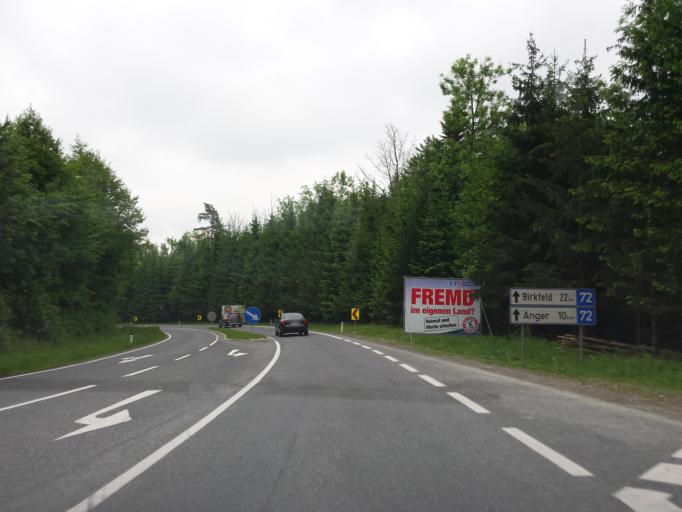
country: AT
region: Styria
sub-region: Politischer Bezirk Weiz
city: Unterfladnitz
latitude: 47.2189
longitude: 15.6660
